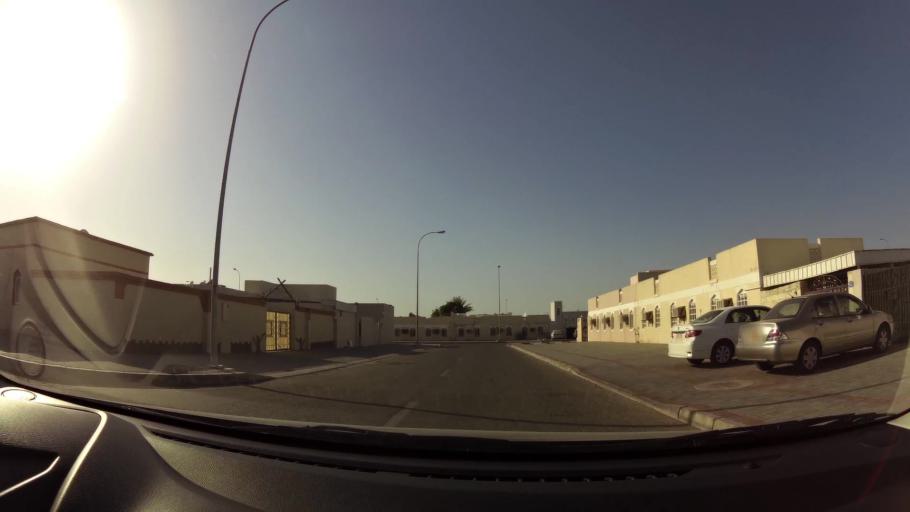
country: OM
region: Muhafazat Masqat
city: As Sib al Jadidah
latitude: 23.6234
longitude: 58.1895
